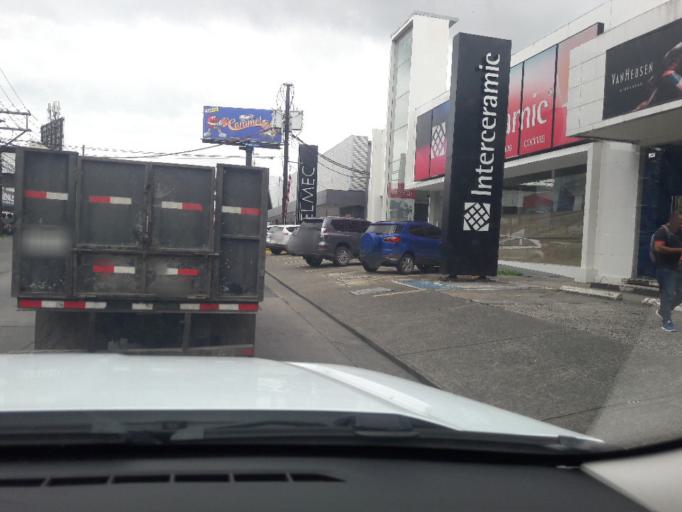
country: PA
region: Panama
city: Panama
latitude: 9.0000
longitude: -79.5199
